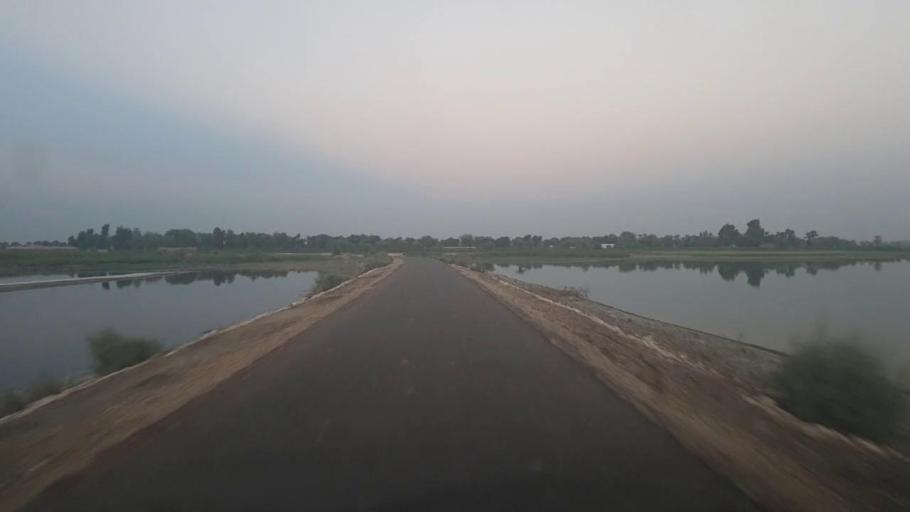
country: PK
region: Sindh
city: Ubauro
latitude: 28.1068
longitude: 69.7743
